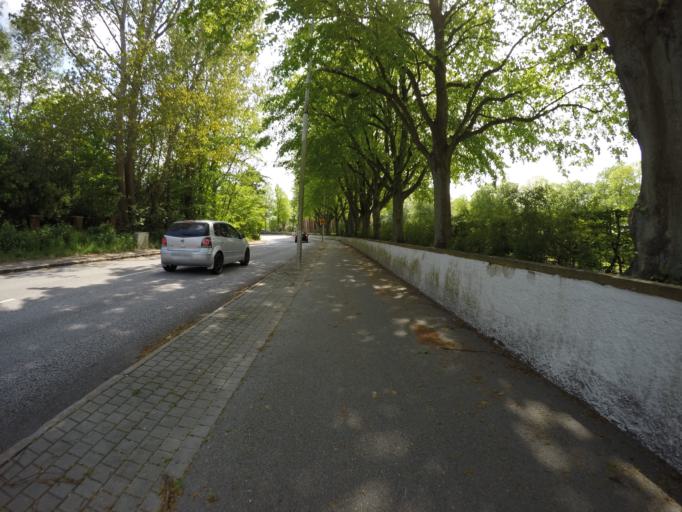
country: SE
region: Skane
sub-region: Malmo
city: Tygelsjo
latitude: 55.5291
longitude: 12.9954
